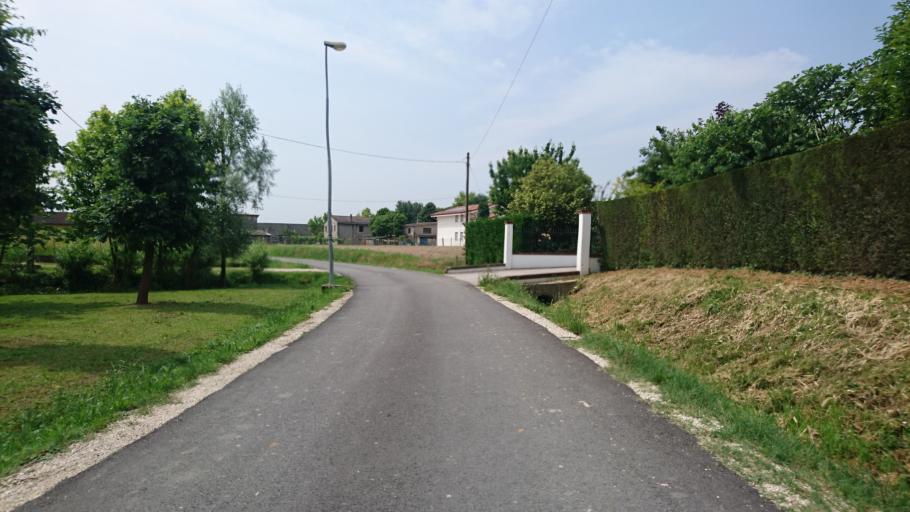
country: IT
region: Veneto
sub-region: Provincia di Padova
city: Polverara
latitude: 45.3107
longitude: 11.9484
